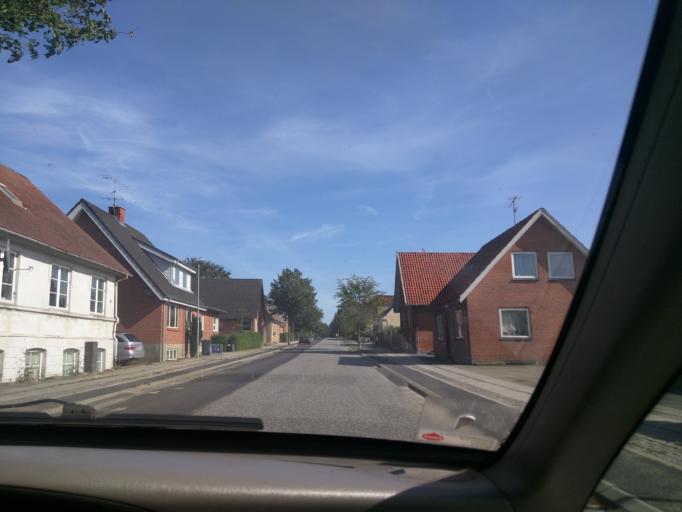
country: DK
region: Central Jutland
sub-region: Favrskov Kommune
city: Hammel
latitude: 56.2684
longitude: 9.7329
